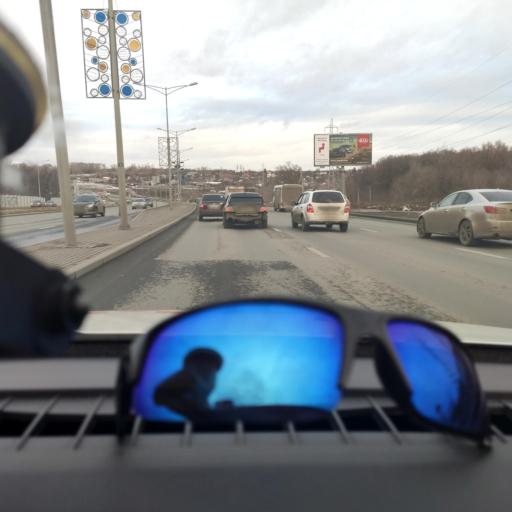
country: RU
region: Samara
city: Petra-Dubrava
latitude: 53.2801
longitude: 50.2779
